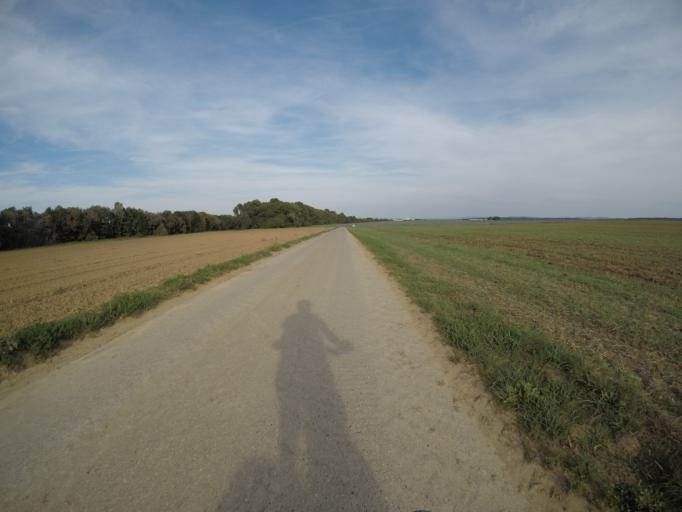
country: DE
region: Baden-Wuerttemberg
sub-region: Regierungsbezirk Stuttgart
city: Ostfildern
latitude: 48.6890
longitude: 9.2449
